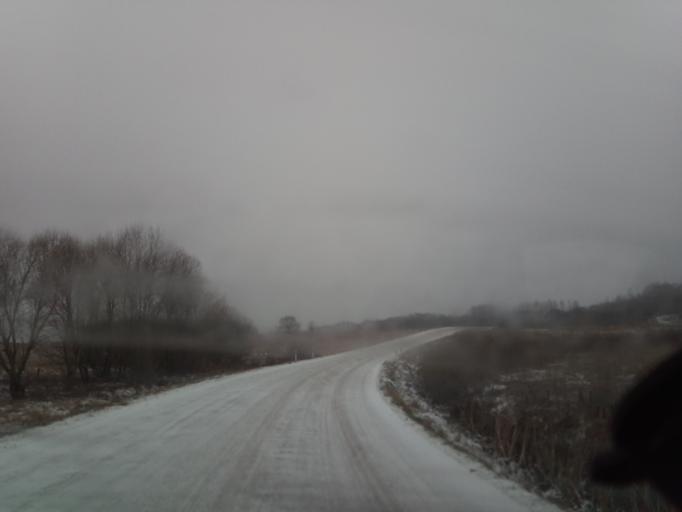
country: LT
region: Utenos apskritis
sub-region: Anyksciai
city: Anyksciai
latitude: 55.4388
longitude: 25.1061
